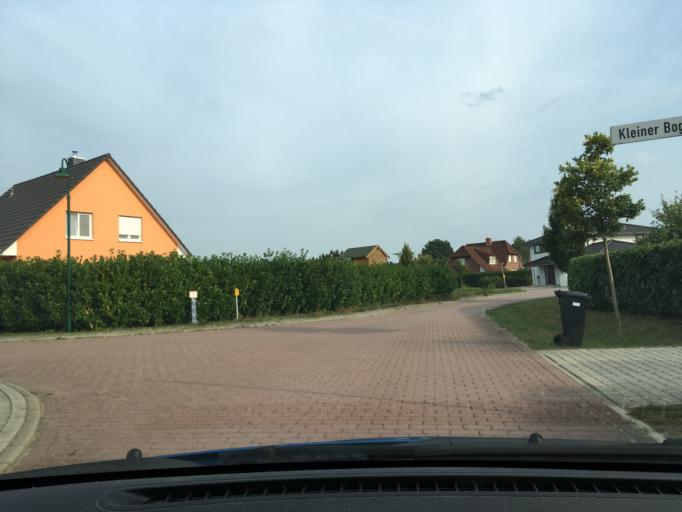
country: DE
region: Lower Saxony
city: Wulfsen
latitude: 53.2917
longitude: 10.1503
